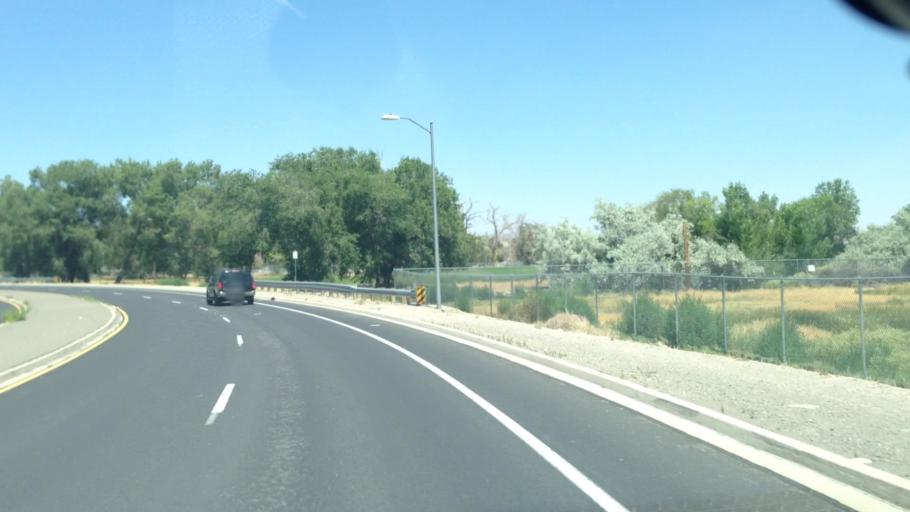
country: US
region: Nevada
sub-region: Washoe County
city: Sparks
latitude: 39.4902
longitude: -119.7761
